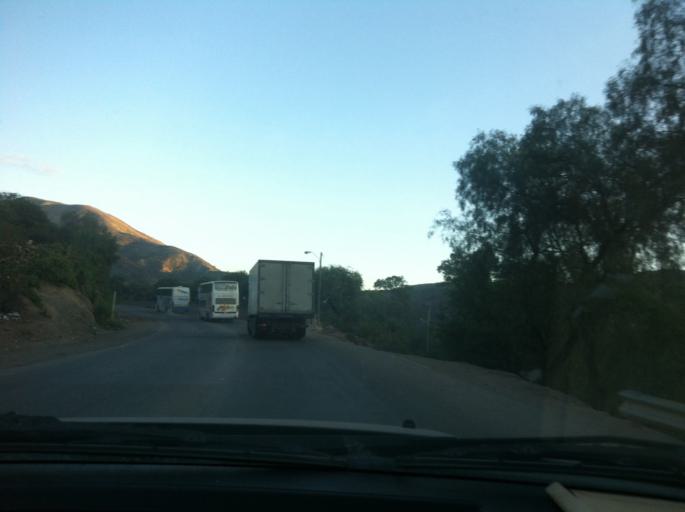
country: BO
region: Cochabamba
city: Sipe Sipe
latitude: -17.5584
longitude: -66.3418
